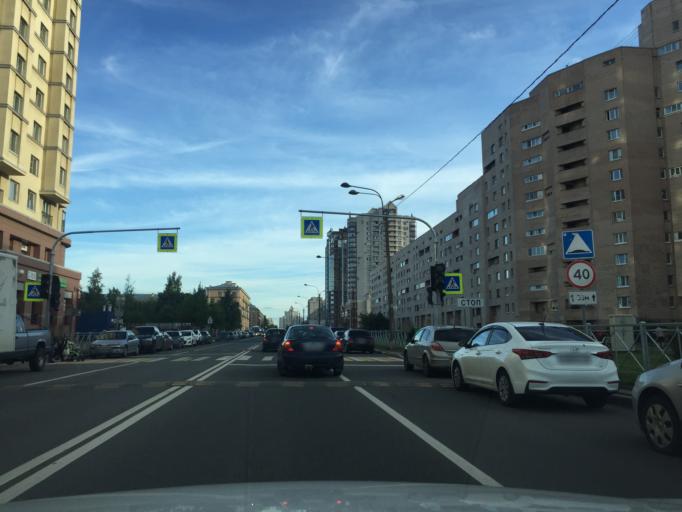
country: RU
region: St.-Petersburg
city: Kupchino
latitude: 59.8555
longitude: 30.3145
